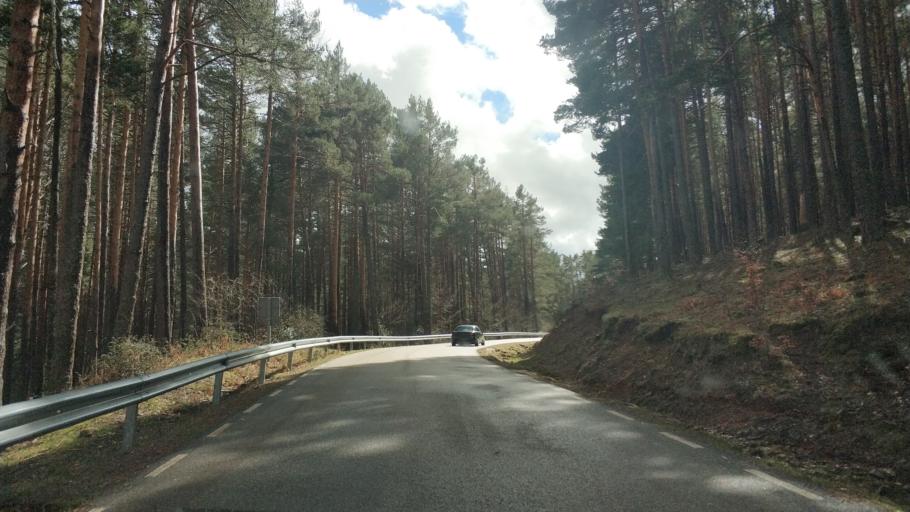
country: ES
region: Castille and Leon
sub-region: Provincia de Burgos
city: Neila
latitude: 42.0522
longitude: -3.0113
